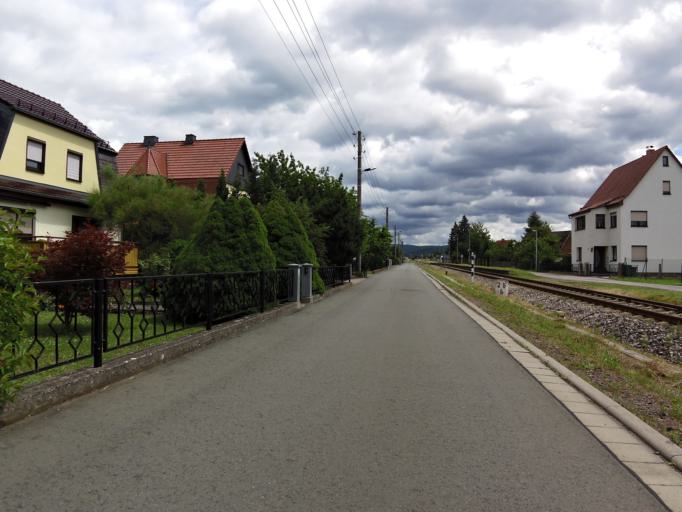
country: DE
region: Thuringia
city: Fambach
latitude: 50.7167
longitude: 10.3736
